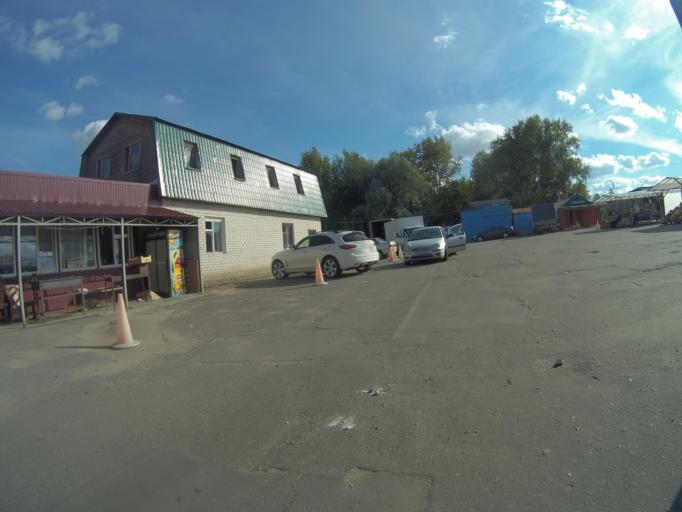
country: RU
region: Vladimir
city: Vladimir
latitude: 56.1406
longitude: 40.3710
